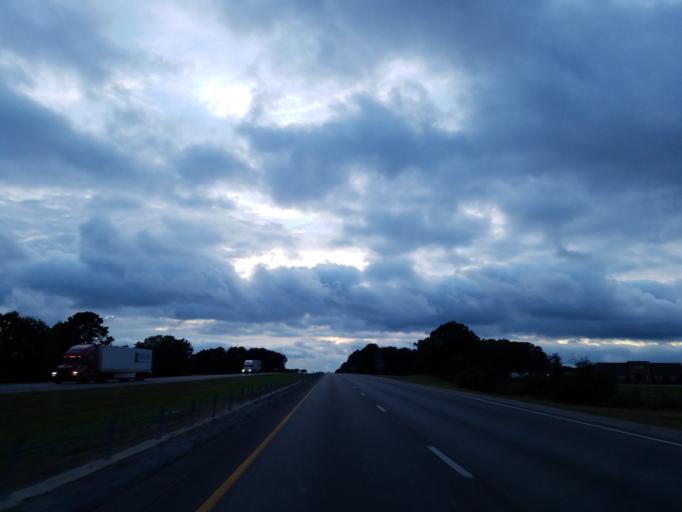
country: US
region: Mississippi
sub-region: Lauderdale County
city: Marion
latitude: 32.3847
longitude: -88.6296
